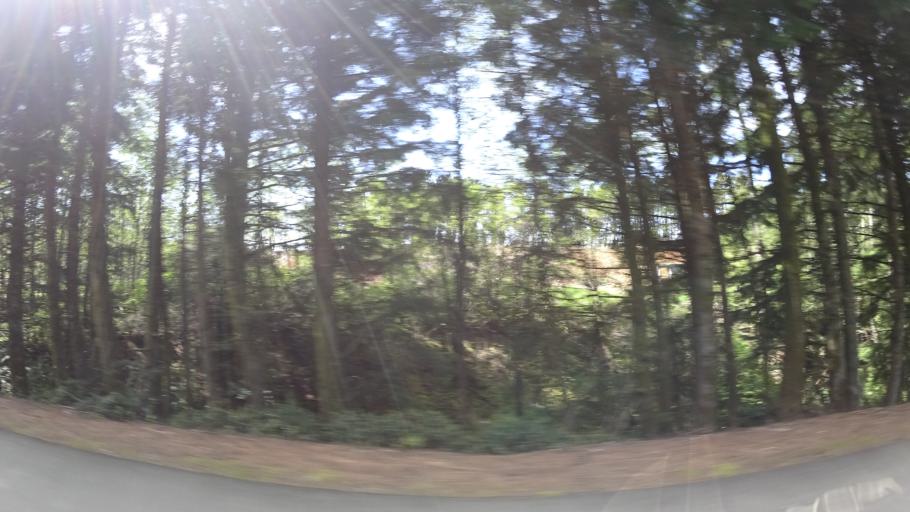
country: US
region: Oregon
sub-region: Lincoln County
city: Lincoln Beach
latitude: 44.8813
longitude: -124.0314
